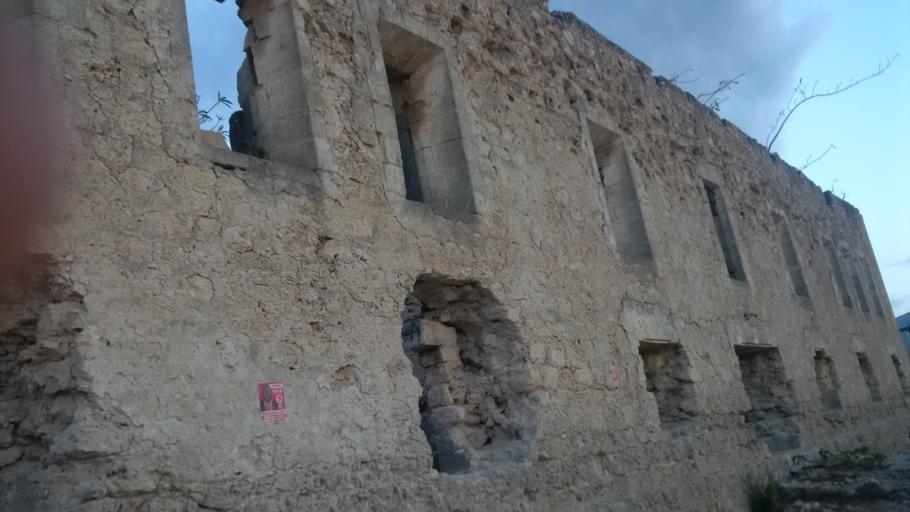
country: HT
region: Nord-Ouest
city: Mole Saint-Nicolas
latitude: 19.8137
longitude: -73.3690
